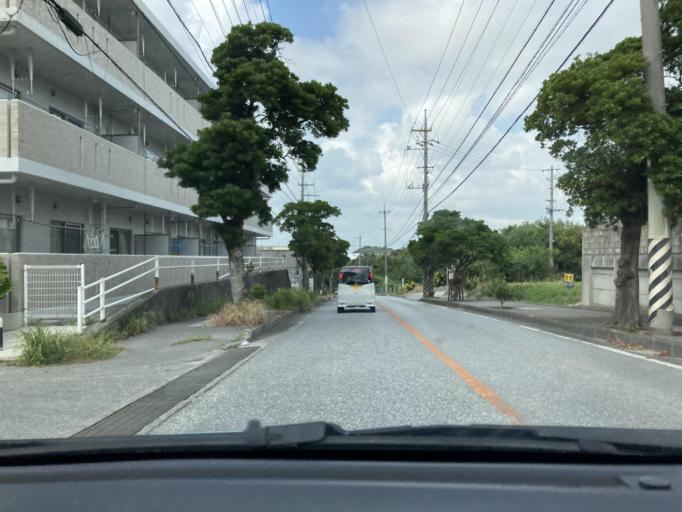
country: JP
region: Okinawa
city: Ginowan
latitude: 26.2576
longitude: 127.7763
